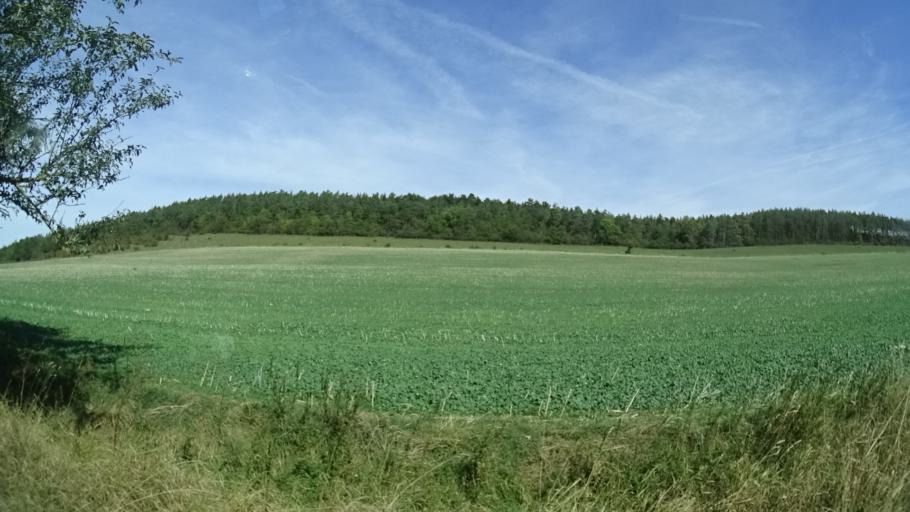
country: DE
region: Thuringia
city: Rottenbach
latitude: 50.7508
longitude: 11.1829
